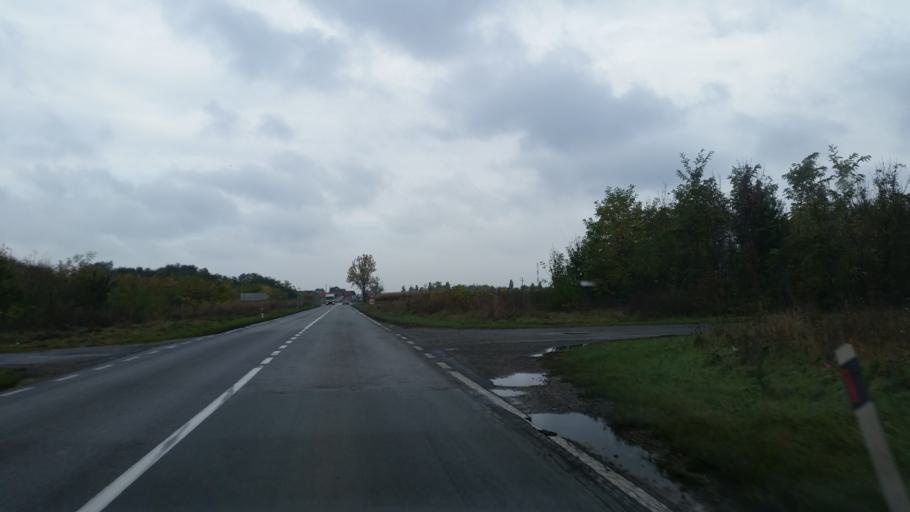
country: RS
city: Ecka
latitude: 45.3288
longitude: 20.4427
